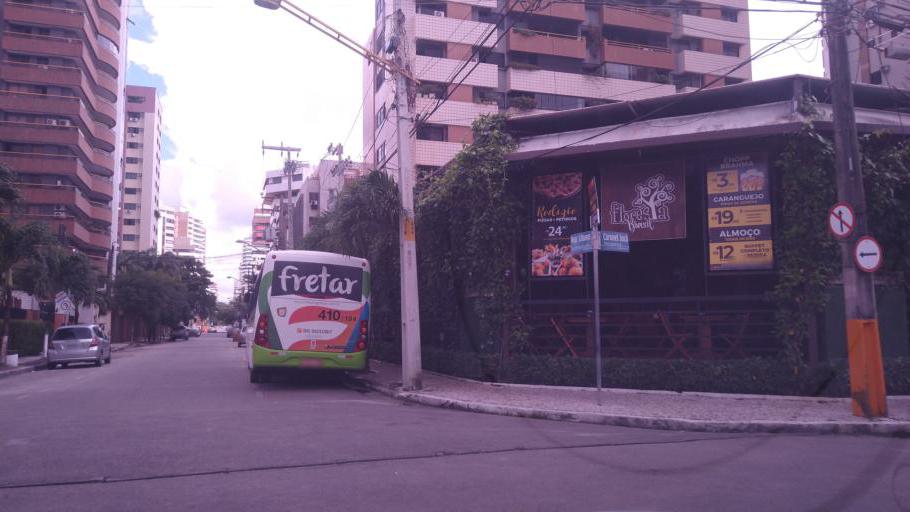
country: BR
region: Ceara
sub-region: Fortaleza
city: Fortaleza
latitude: -3.7335
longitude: -38.4899
